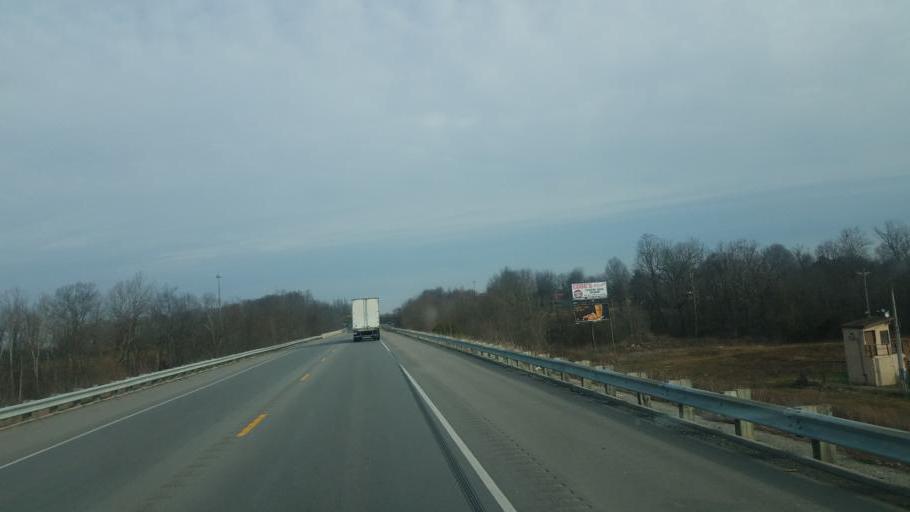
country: US
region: Kentucky
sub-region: Boyle County
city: Junction City
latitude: 37.5665
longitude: -84.7968
